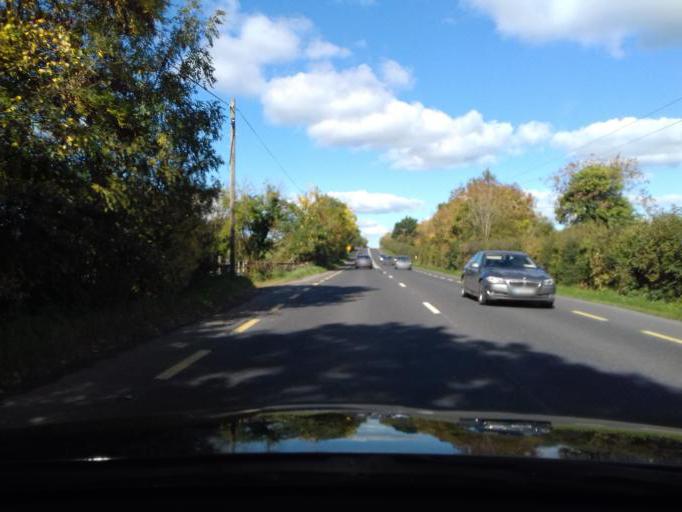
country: IE
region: Leinster
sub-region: An Mhi
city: Slane
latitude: 53.6729
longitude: -6.5348
